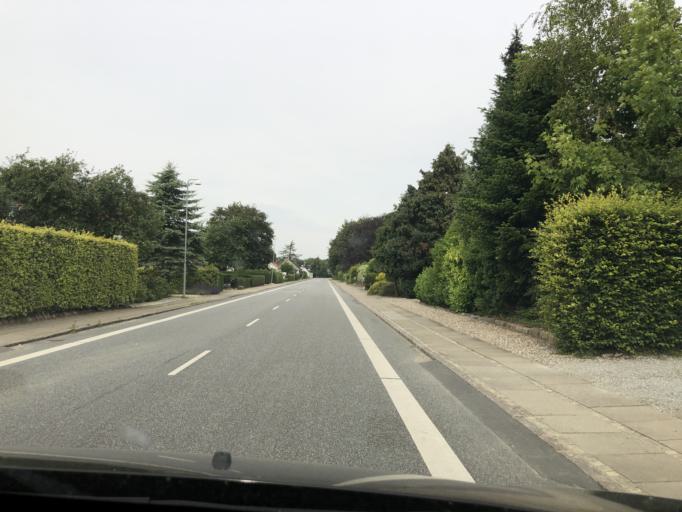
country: DK
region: South Denmark
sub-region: Assens Kommune
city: Glamsbjerg
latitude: 55.2827
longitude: 10.0979
